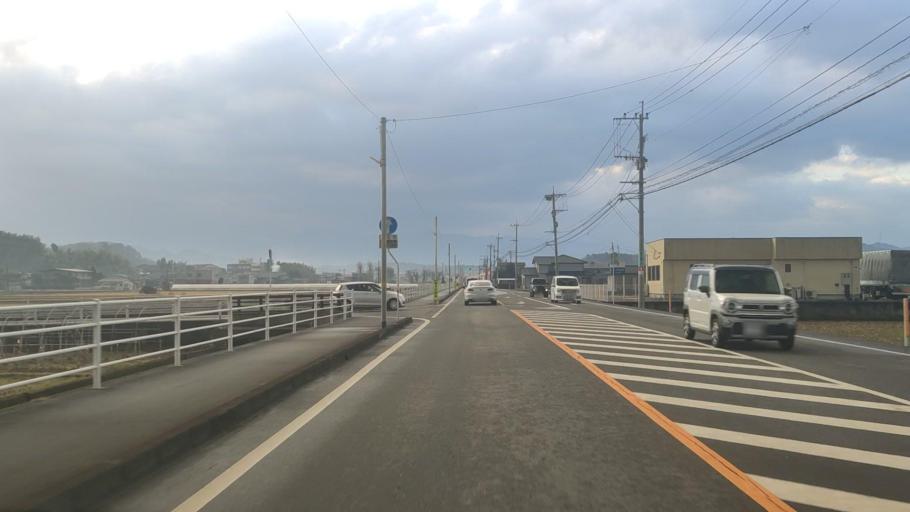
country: JP
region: Kumamoto
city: Uto
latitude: 32.7069
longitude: 130.7768
